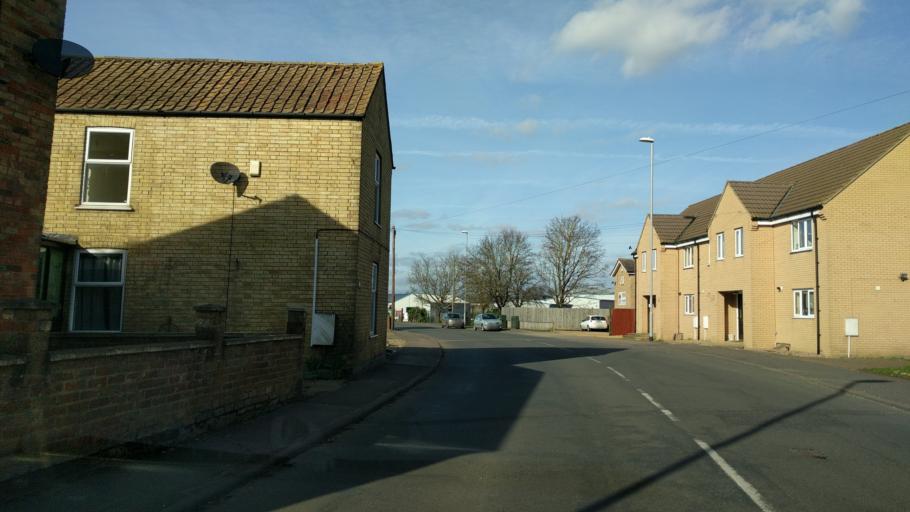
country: GB
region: England
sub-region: Cambridgeshire
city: Chatteris
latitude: 52.4622
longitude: 0.0454
